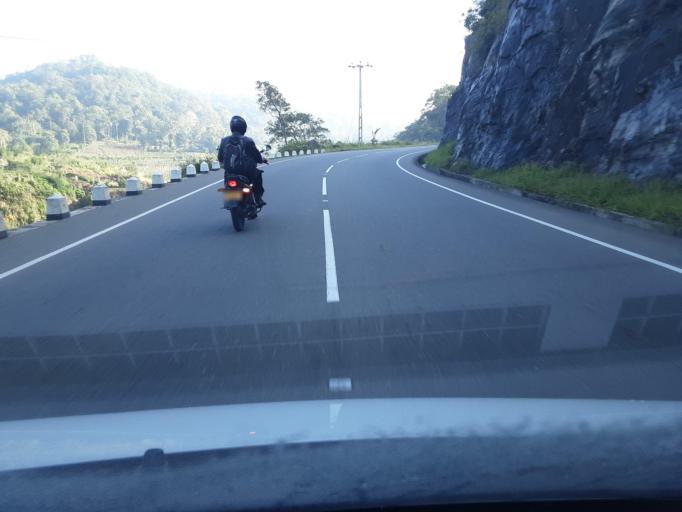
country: LK
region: Uva
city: Haputale
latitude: 6.9090
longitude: 80.9273
